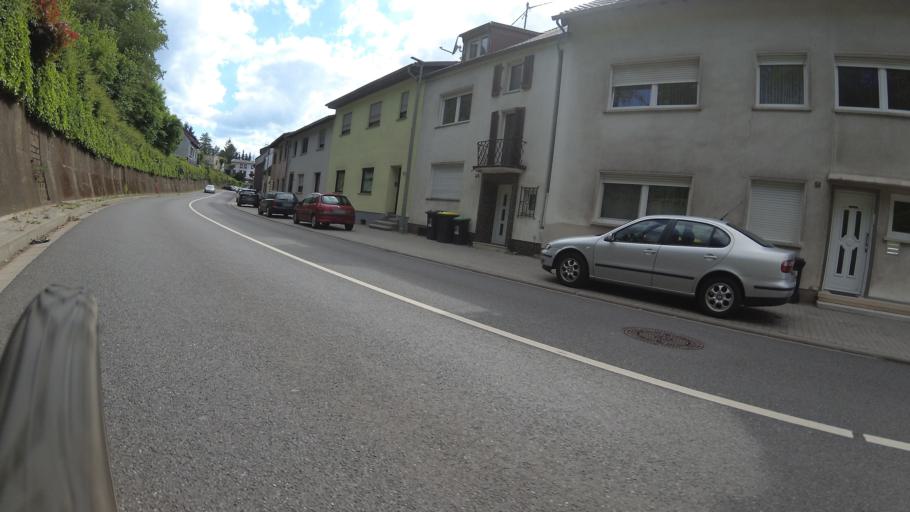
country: DE
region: Saarland
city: Puttlingen
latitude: 49.2905
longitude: 6.8889
